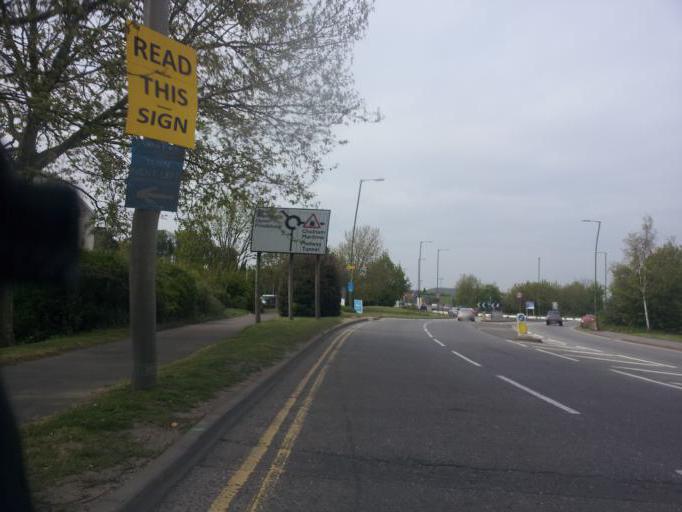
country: GB
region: England
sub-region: Medway
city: Rochester
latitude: 51.4002
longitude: 0.5144
